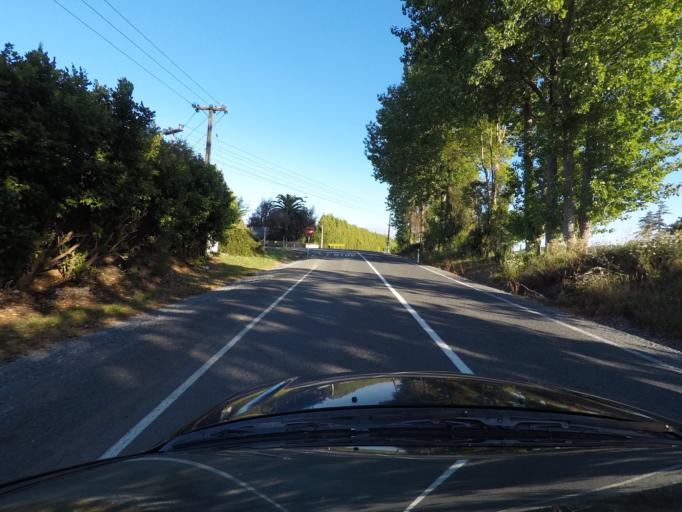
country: NZ
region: Northland
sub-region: Whangarei
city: Whangarei
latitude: -35.6400
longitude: 174.2972
